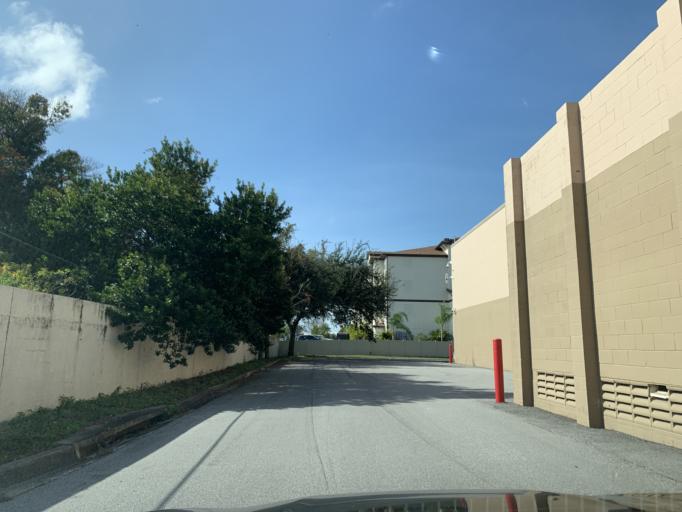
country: US
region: Florida
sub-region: Hillsborough County
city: Tampa
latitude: 27.8889
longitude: -82.5097
